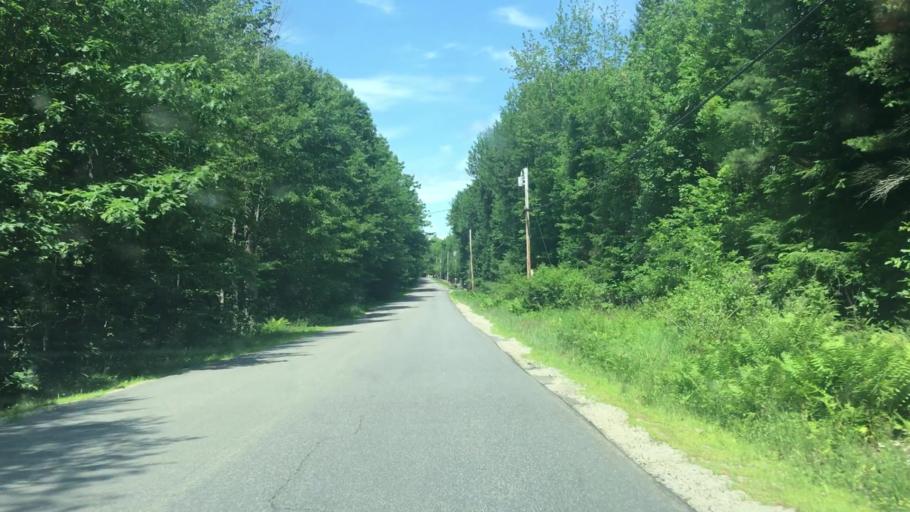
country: US
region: Maine
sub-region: Kennebec County
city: Monmouth
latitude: 44.2799
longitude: -70.0529
